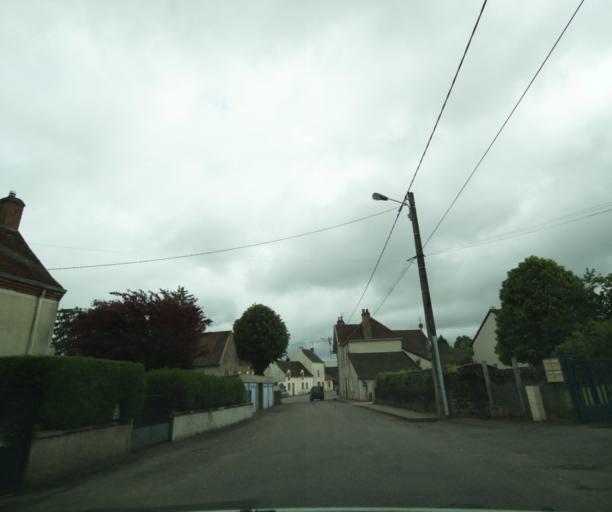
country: FR
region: Bourgogne
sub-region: Departement de Saone-et-Loire
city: Charolles
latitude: 46.4337
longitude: 4.2693
